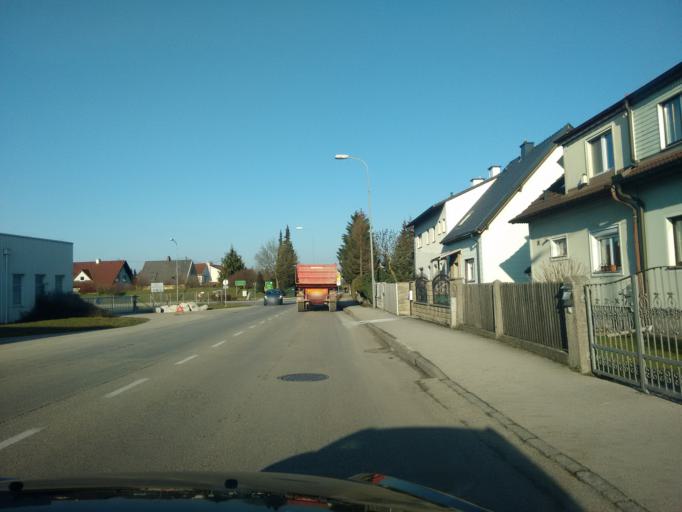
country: AT
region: Upper Austria
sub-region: Wels-Land
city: Marchtrenk
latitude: 48.1932
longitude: 14.0918
